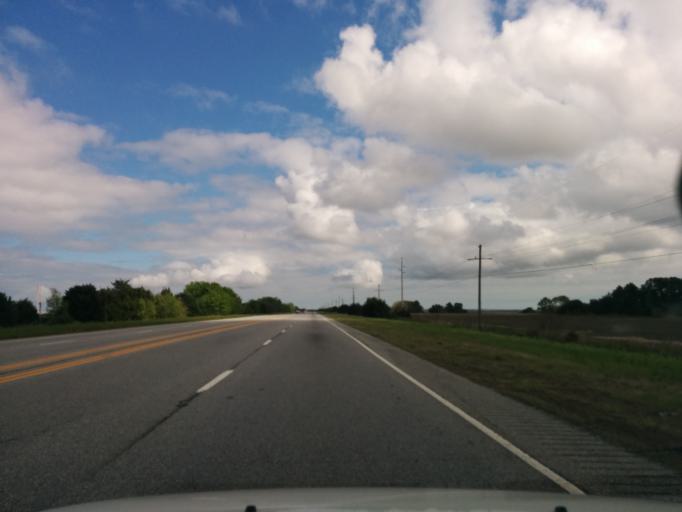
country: US
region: Georgia
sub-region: Glynn County
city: Brunswick
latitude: 31.1106
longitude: -81.5201
